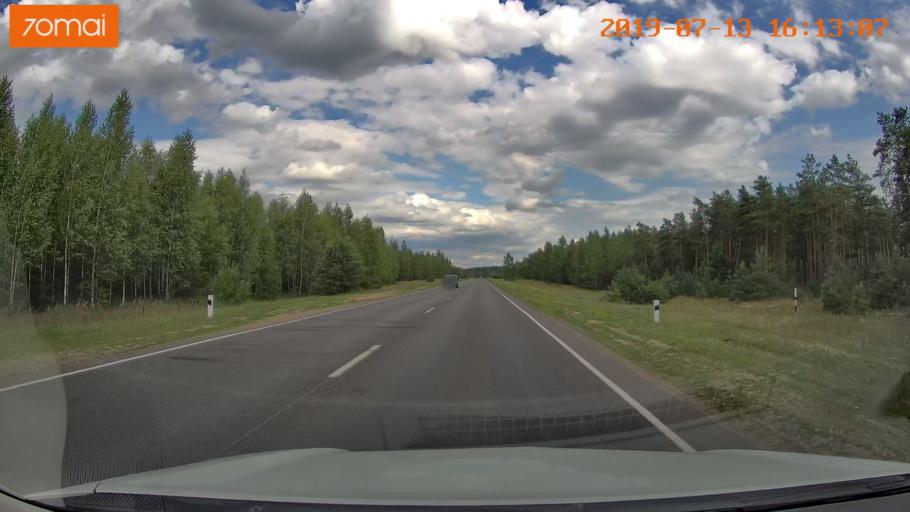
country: BY
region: Mogilev
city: Babruysk
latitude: 53.1643
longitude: 29.2958
